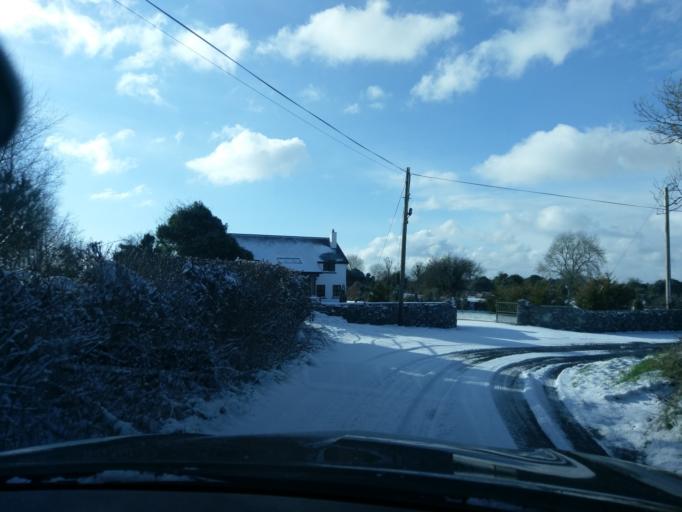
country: IE
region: Connaught
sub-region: County Galway
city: Athenry
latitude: 53.2057
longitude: -8.8126
